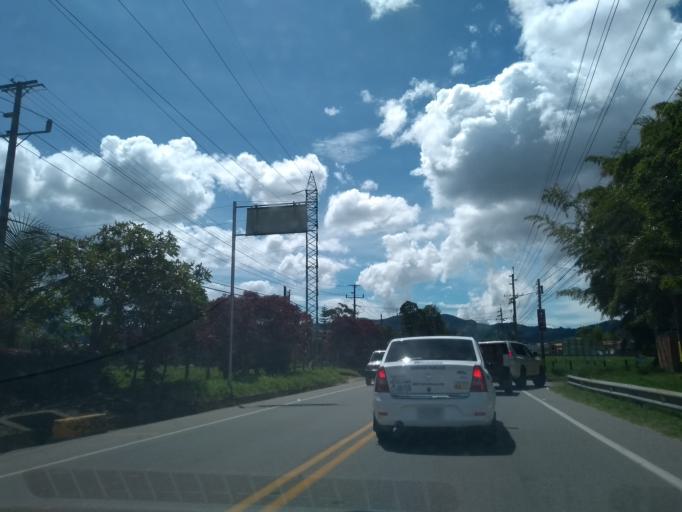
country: CO
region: Antioquia
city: La Ceja
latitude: 6.0392
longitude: -75.4174
